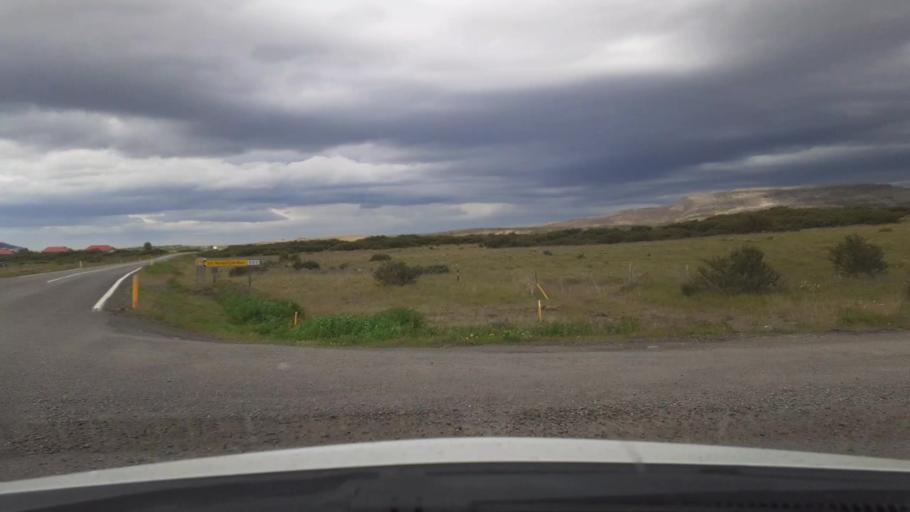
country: IS
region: West
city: Borgarnes
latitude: 64.5431
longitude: -21.6196
